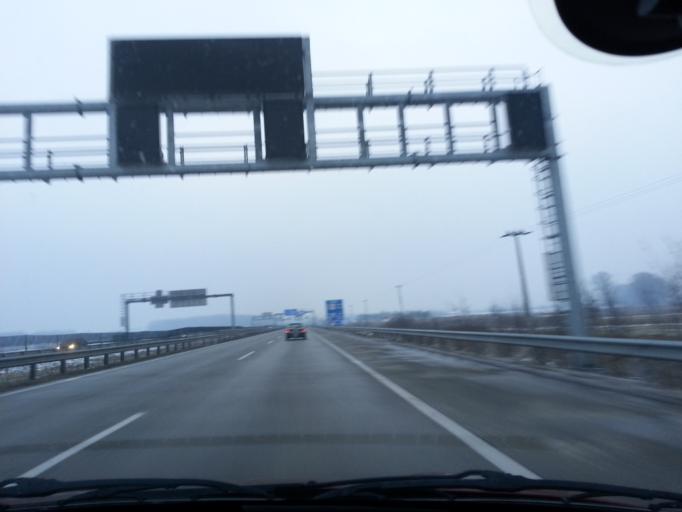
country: HU
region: Pest
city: Gyal
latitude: 47.3737
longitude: 19.2532
